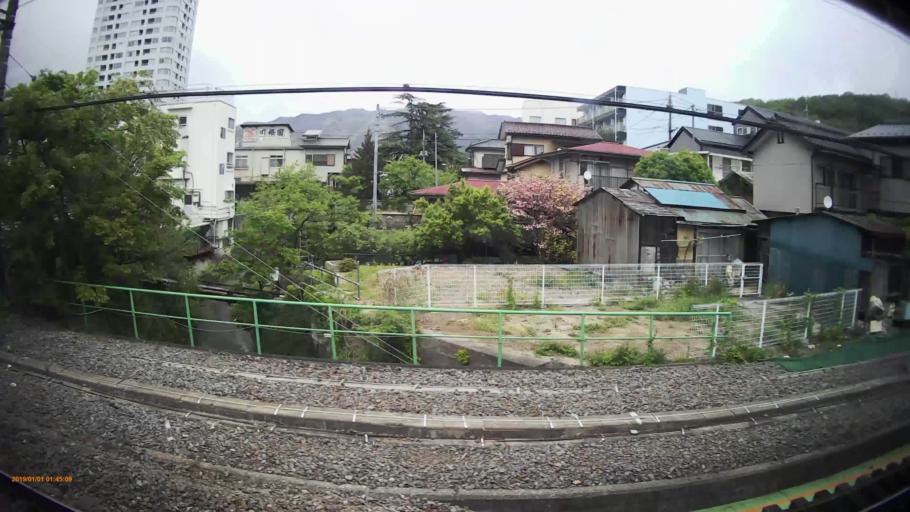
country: JP
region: Yamanashi
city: Kofu-shi
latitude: 35.6662
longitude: 138.5734
